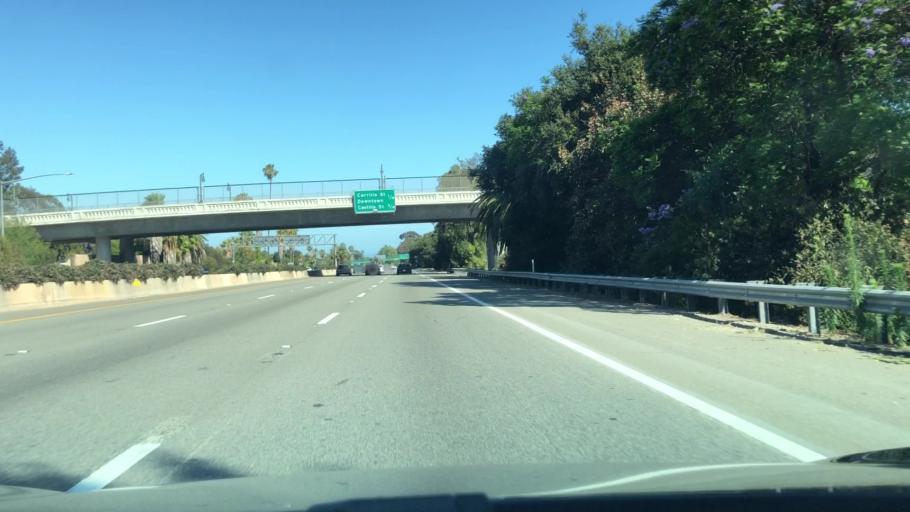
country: US
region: California
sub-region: Santa Barbara County
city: Santa Barbara
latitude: 34.4214
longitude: -119.7149
